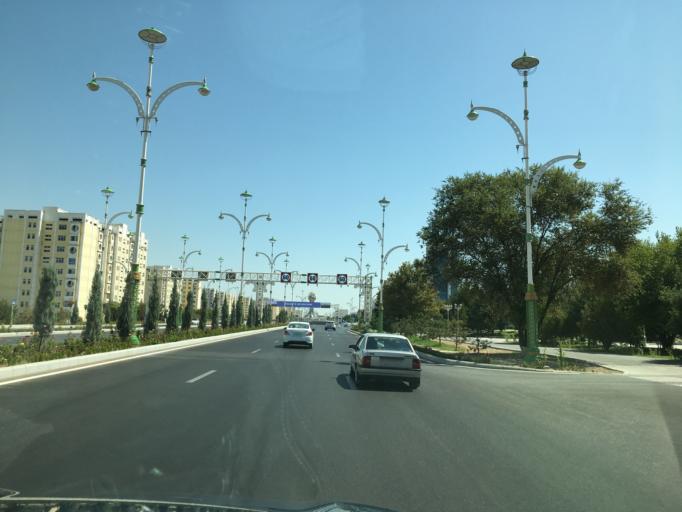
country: TM
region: Ahal
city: Ashgabat
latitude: 37.8955
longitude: 58.3828
